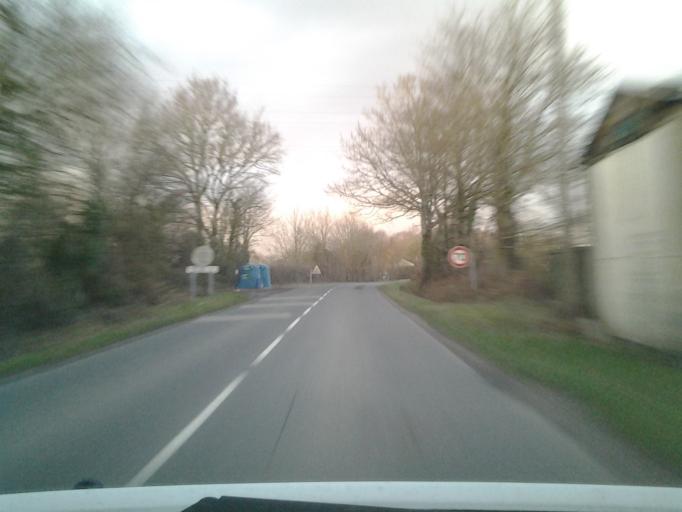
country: FR
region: Pays de la Loire
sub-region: Departement de la Vendee
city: La Roche-sur-Yon
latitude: 46.6401
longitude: -1.4576
